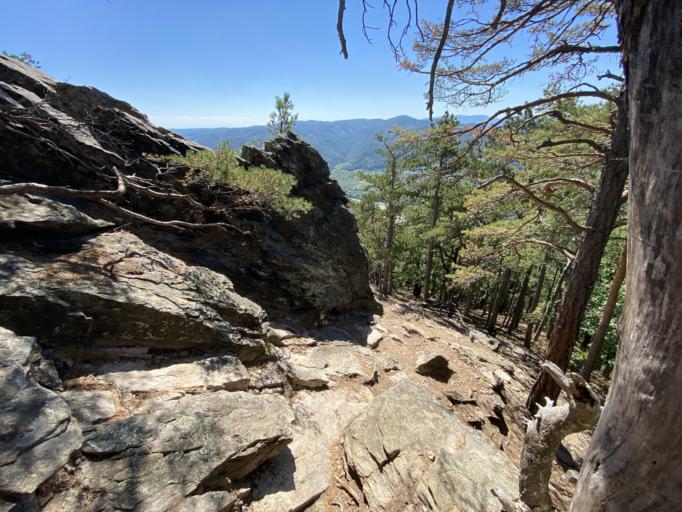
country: AT
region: Lower Austria
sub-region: Politischer Bezirk Krems
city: Durnstein
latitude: 48.4028
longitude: 15.5285
